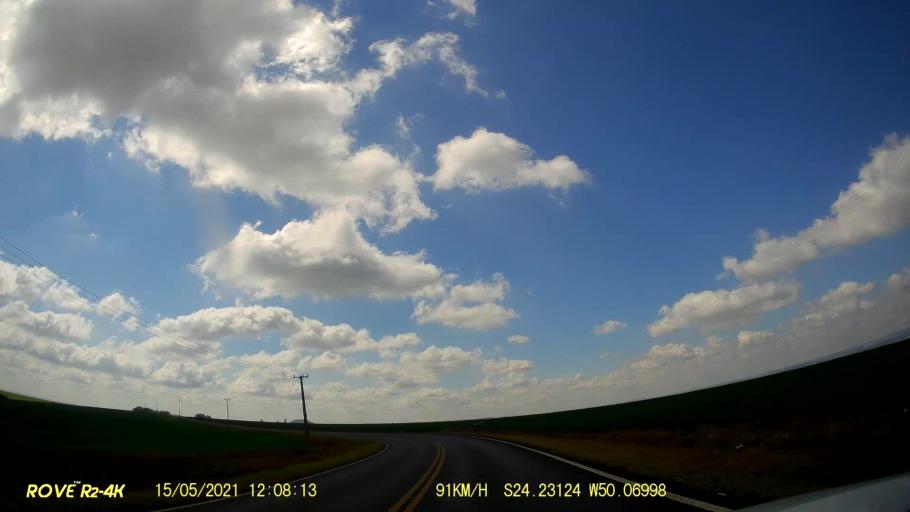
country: BR
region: Parana
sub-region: Pirai Do Sul
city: Pirai do Sul
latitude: -24.2317
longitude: -50.0697
